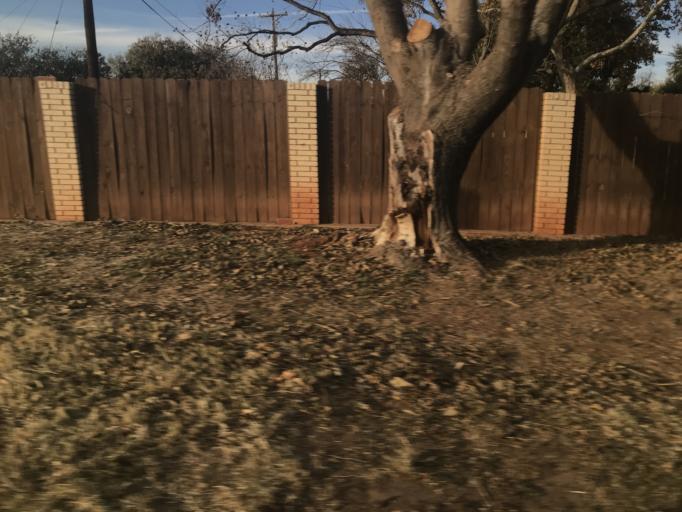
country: US
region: Texas
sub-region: Taylor County
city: Abilene
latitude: 32.4324
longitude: -99.7765
